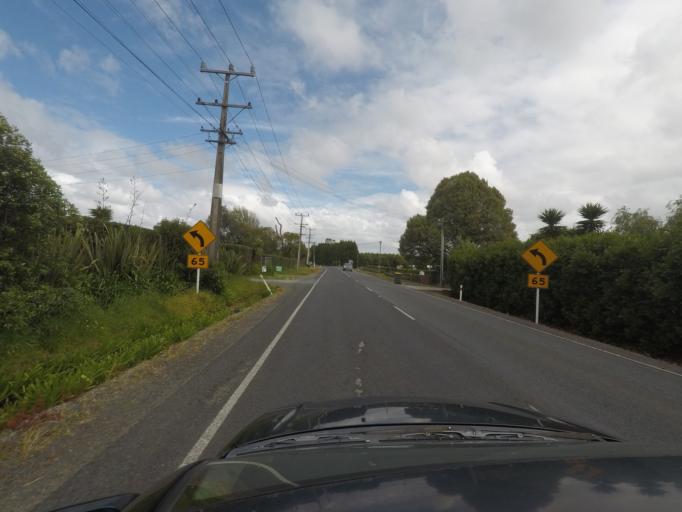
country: NZ
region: Auckland
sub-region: Auckland
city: Muriwai Beach
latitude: -36.7721
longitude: 174.5735
